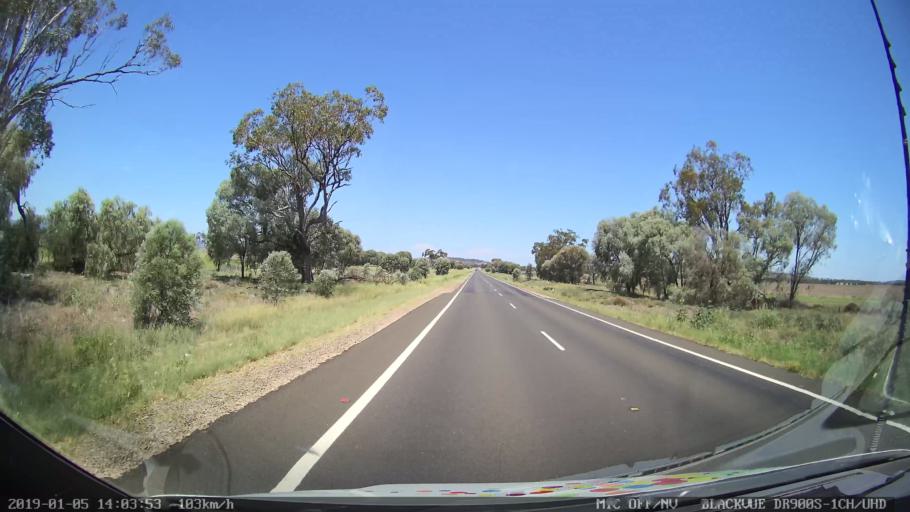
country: AU
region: New South Wales
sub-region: Gunnedah
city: Gunnedah
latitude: -31.1944
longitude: 150.3567
